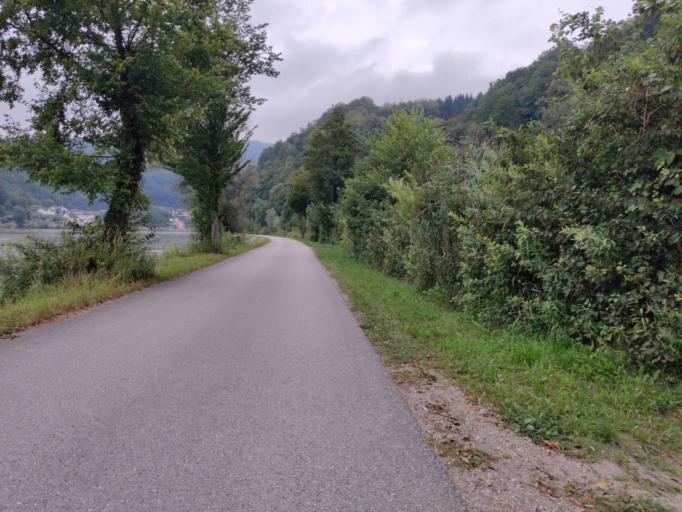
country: AT
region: Lower Austria
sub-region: Politischer Bezirk Melk
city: Nochling
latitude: 48.2277
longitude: 14.8987
